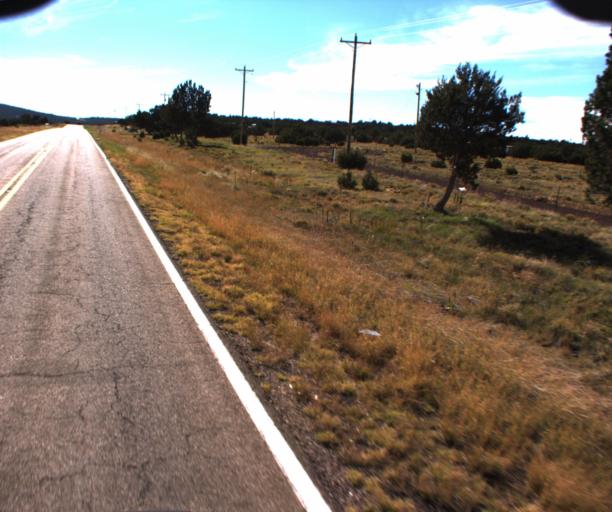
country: US
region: Arizona
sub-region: Navajo County
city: White Mountain Lake
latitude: 34.3337
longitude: -109.7420
